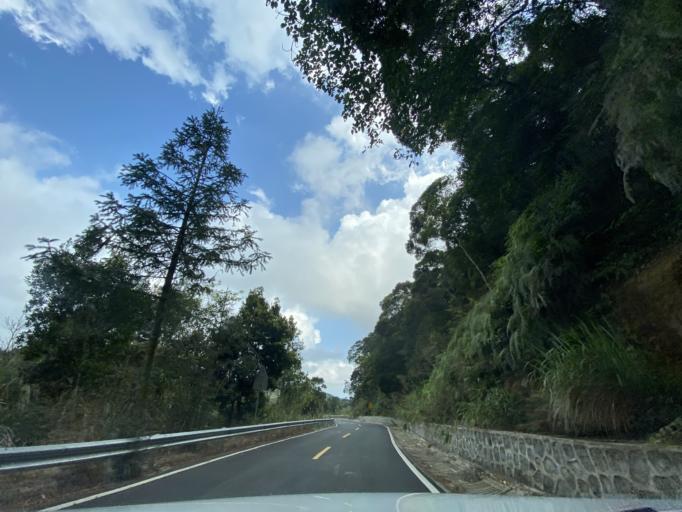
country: CN
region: Hainan
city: Diaoluoshan
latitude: 18.7212
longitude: 109.8748
